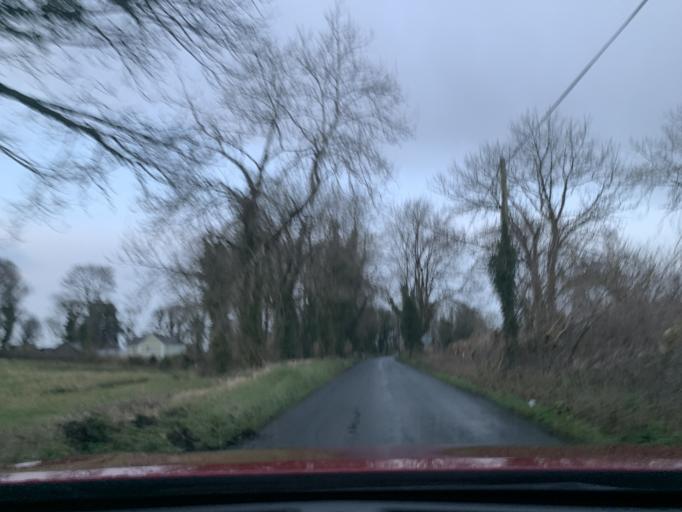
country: IE
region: Connaught
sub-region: Sligo
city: Ballymote
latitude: 54.0371
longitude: -8.6133
